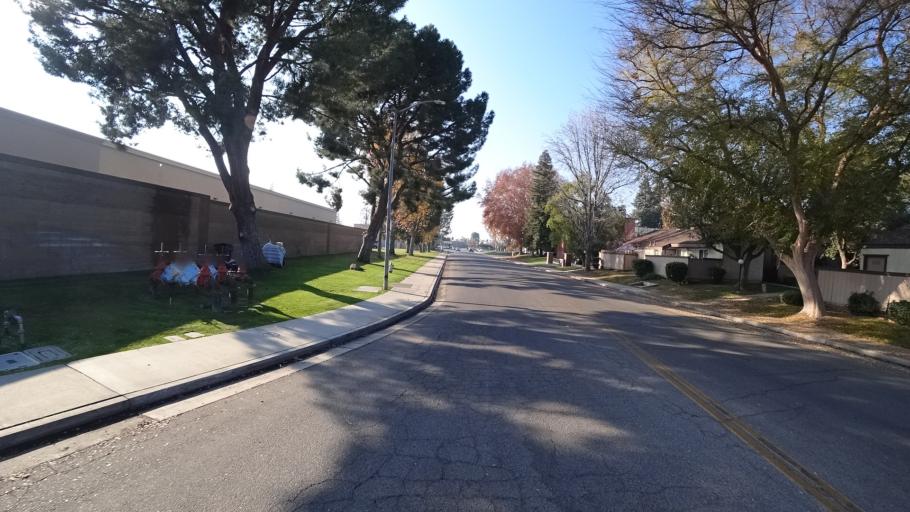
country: US
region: California
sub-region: Kern County
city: Bakersfield
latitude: 35.3563
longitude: -119.0591
